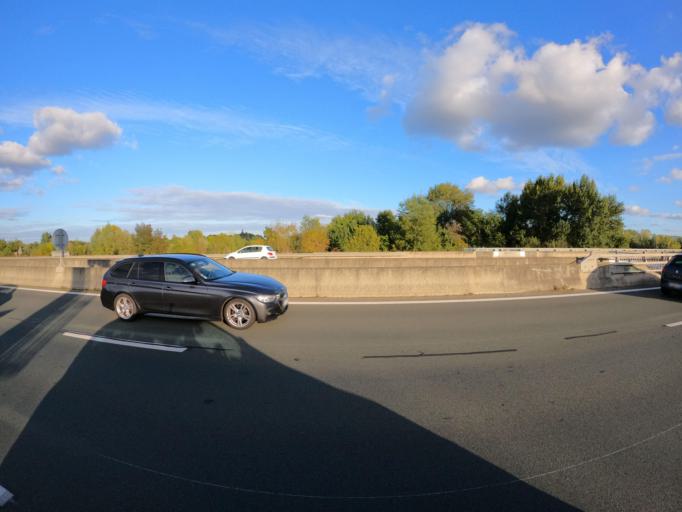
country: FR
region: Pays de la Loire
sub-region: Departement de Maine-et-Loire
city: Les Ponts-de-Ce
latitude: 47.4210
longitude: -0.5046
